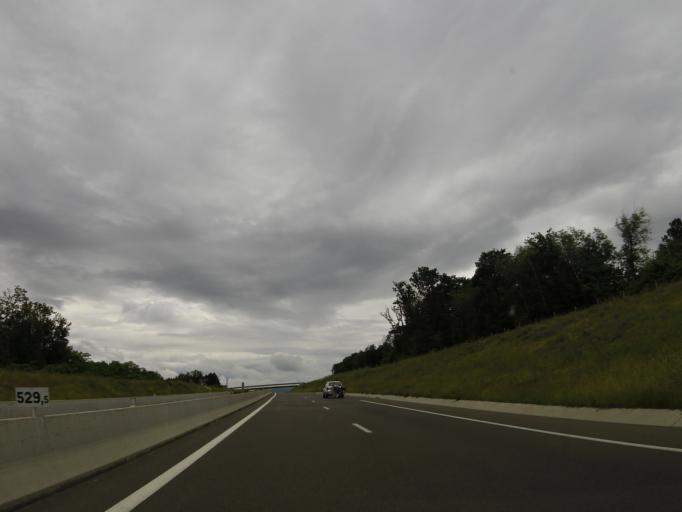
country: FR
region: Rhone-Alpes
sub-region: Departement du Rhone
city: Saint-Germain-Nuelles
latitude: 45.8658
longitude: 4.6110
